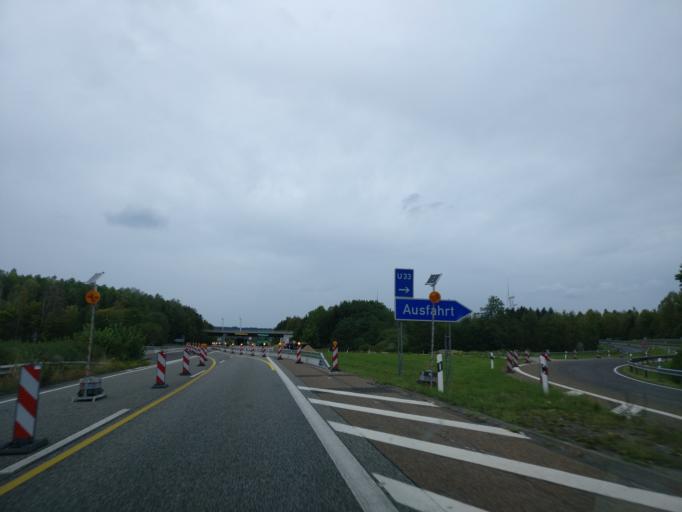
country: DE
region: Rheinland-Pfalz
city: Hermeskeil
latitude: 49.6737
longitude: 6.9188
